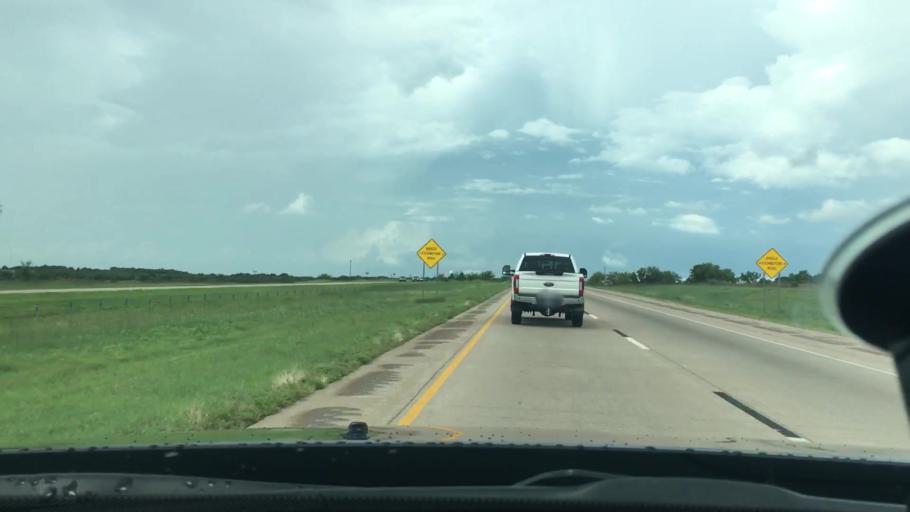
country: US
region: Oklahoma
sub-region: Garvin County
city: Pauls Valley
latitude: 34.6779
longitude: -97.2267
